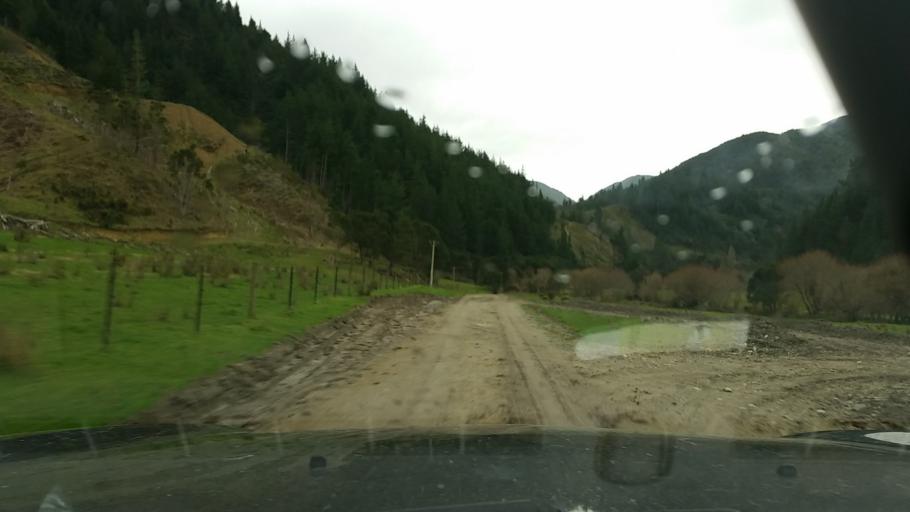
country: NZ
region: Marlborough
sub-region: Marlborough District
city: Blenheim
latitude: -41.3921
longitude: 173.8496
